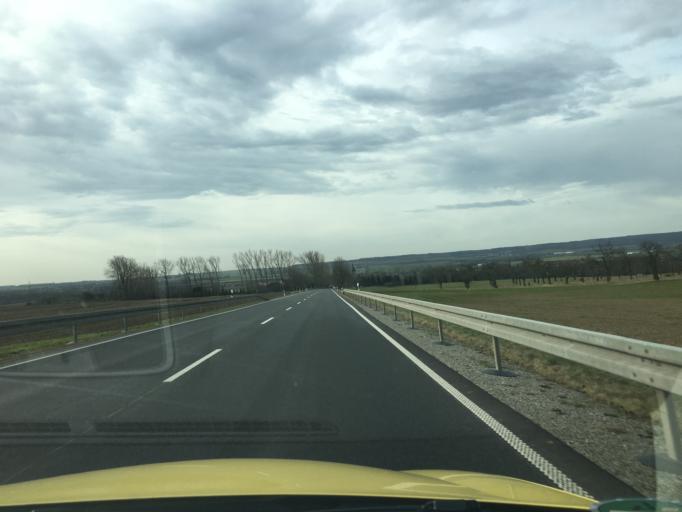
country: DE
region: Thuringia
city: Buttelstedt
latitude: 51.0855
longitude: 11.3485
